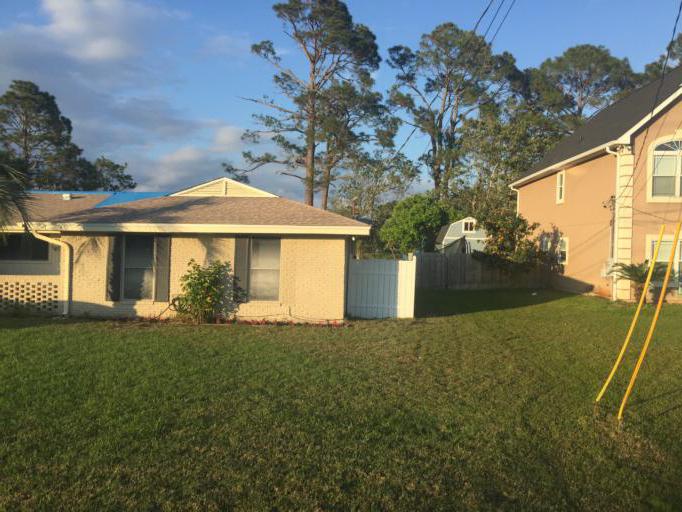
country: US
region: Florida
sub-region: Bay County
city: Panama City Beach
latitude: 30.2104
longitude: -85.8432
